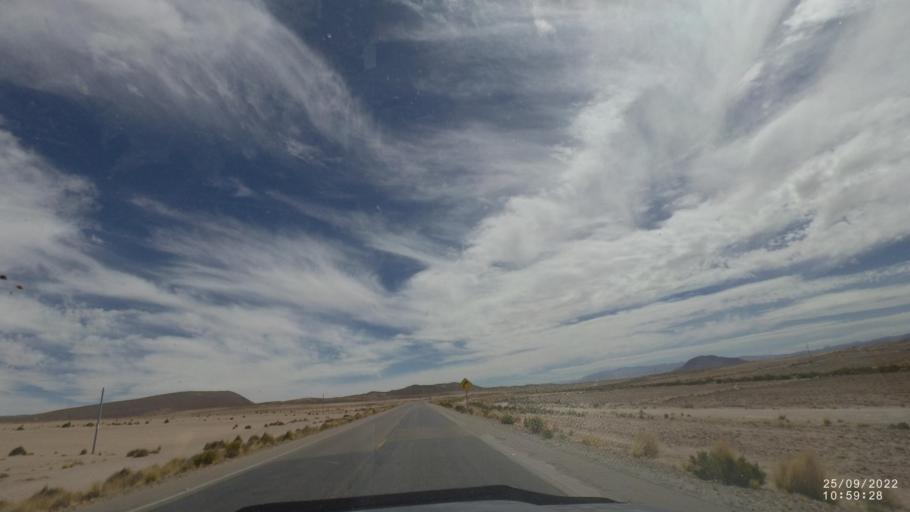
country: BO
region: Oruro
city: Challapata
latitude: -19.4481
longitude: -66.9097
